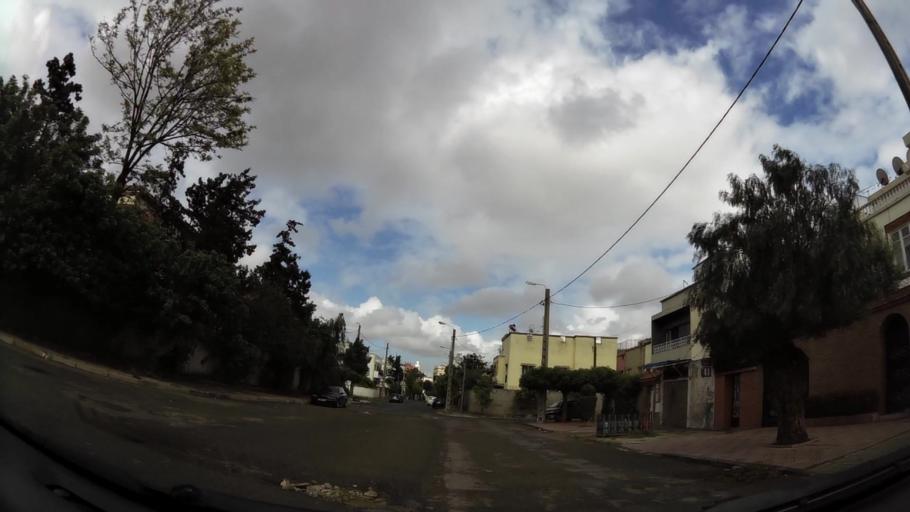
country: MA
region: Grand Casablanca
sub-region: Casablanca
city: Casablanca
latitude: 33.5554
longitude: -7.6081
